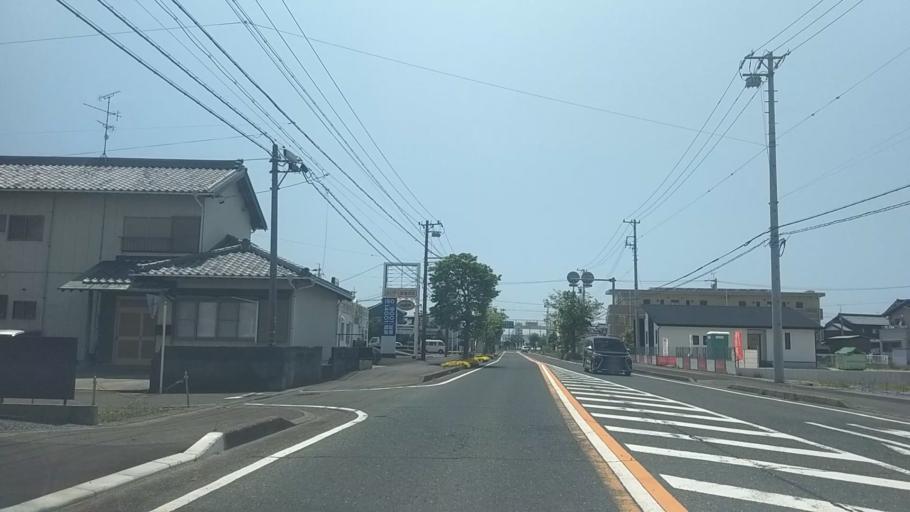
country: JP
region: Shizuoka
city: Hamamatsu
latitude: 34.6855
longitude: 137.6705
